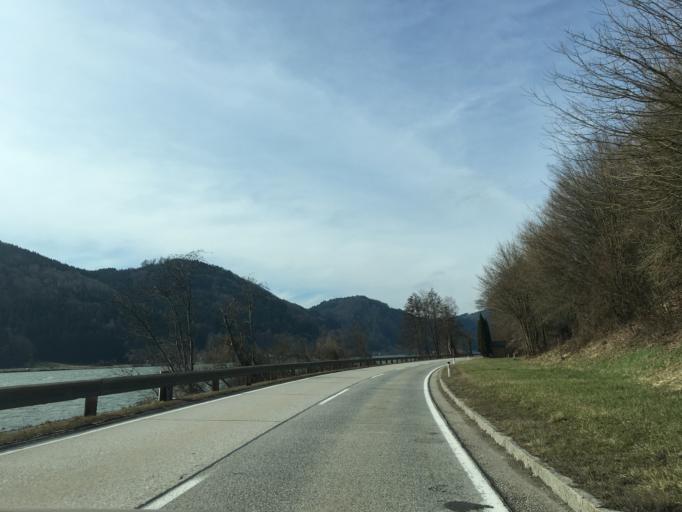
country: AT
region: Lower Austria
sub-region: Politischer Bezirk Melk
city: Nochling
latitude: 48.1984
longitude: 14.9804
